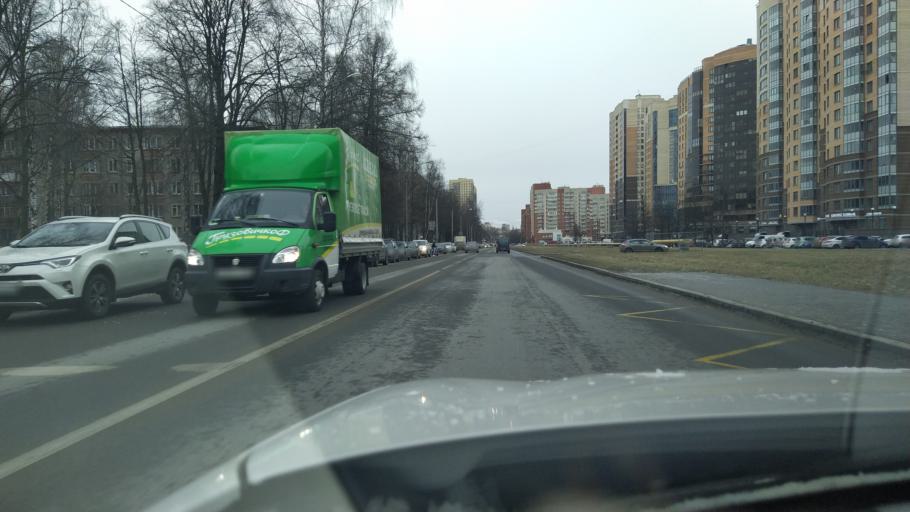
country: RU
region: Leningrad
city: Akademicheskoe
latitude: 60.0037
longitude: 30.3985
